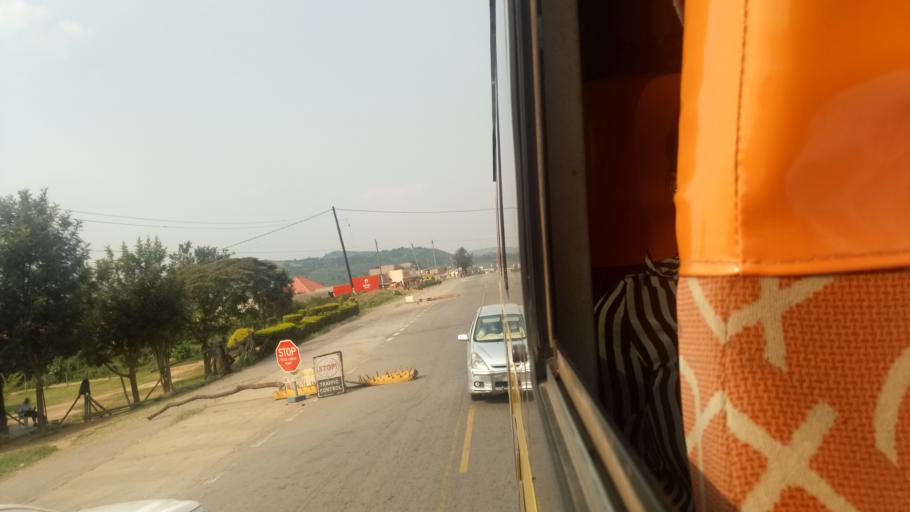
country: UG
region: Western Region
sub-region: Mbarara District
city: Mbarara
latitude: -0.5258
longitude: 30.7293
